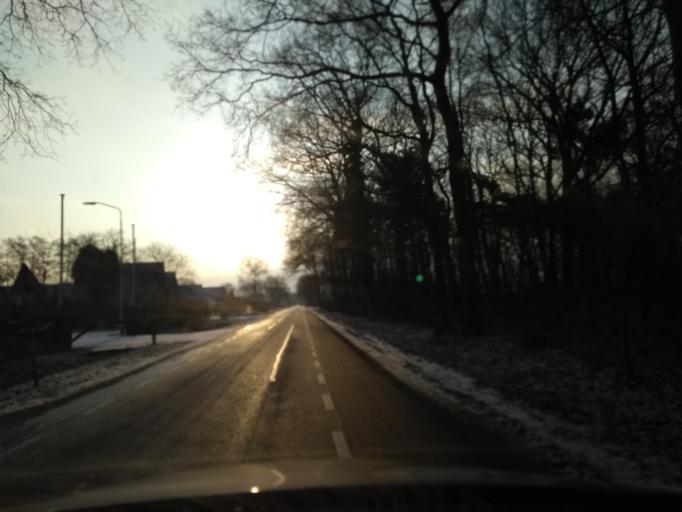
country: NL
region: Overijssel
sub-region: Gemeente Hof van Twente
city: Delden
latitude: 52.2241
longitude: 6.6988
